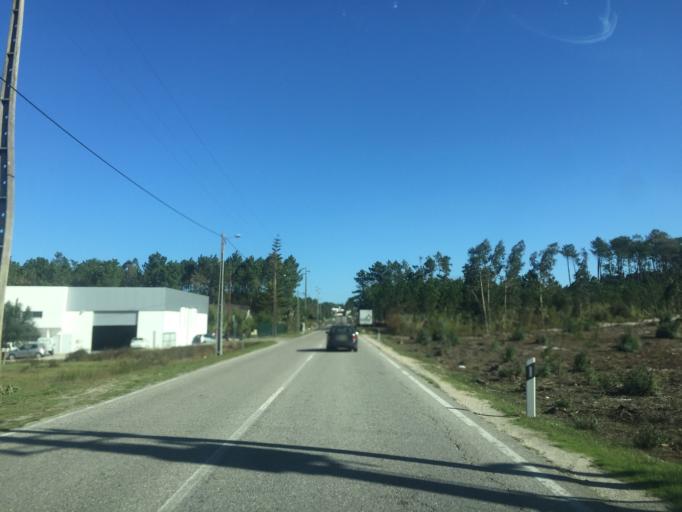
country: PT
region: Leiria
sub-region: Leiria
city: Monte Redondo
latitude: 39.9385
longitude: -8.7963
